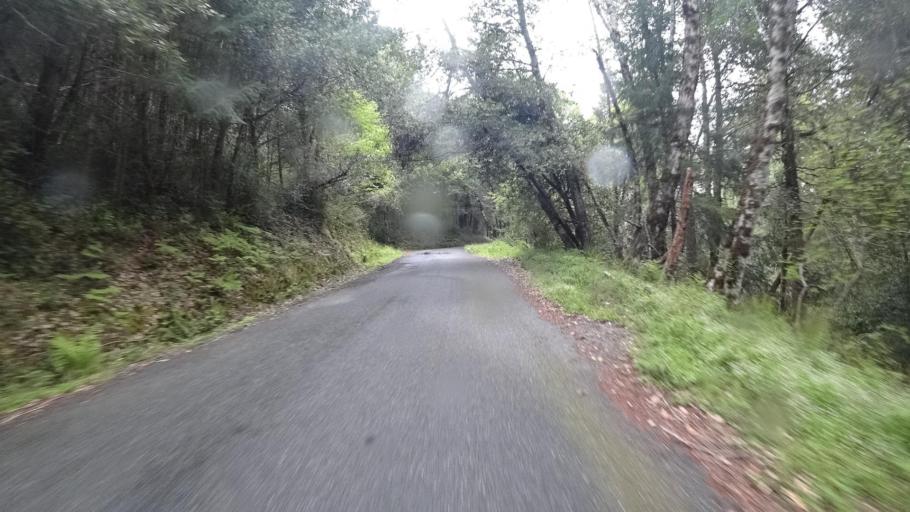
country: US
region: California
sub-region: Humboldt County
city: Willow Creek
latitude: 41.1985
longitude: -123.7703
